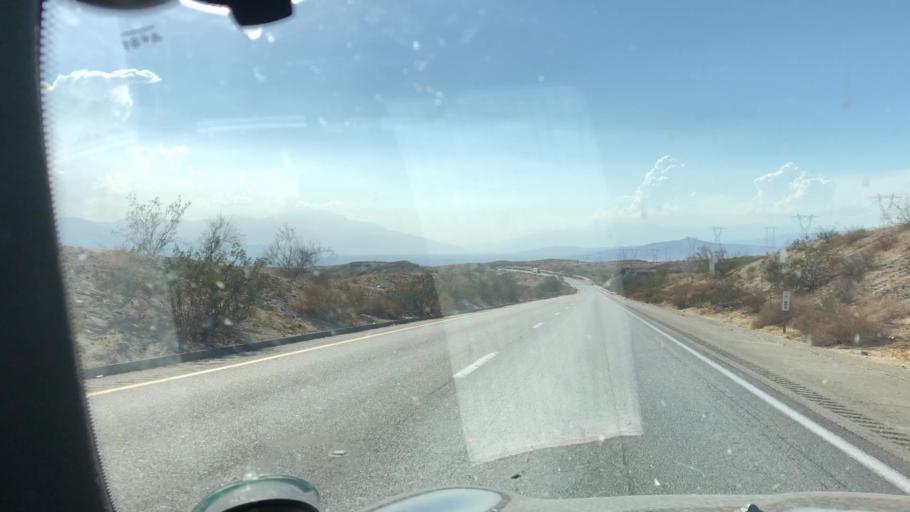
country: US
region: California
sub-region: Riverside County
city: Thermal
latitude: 33.6964
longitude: -116.0577
